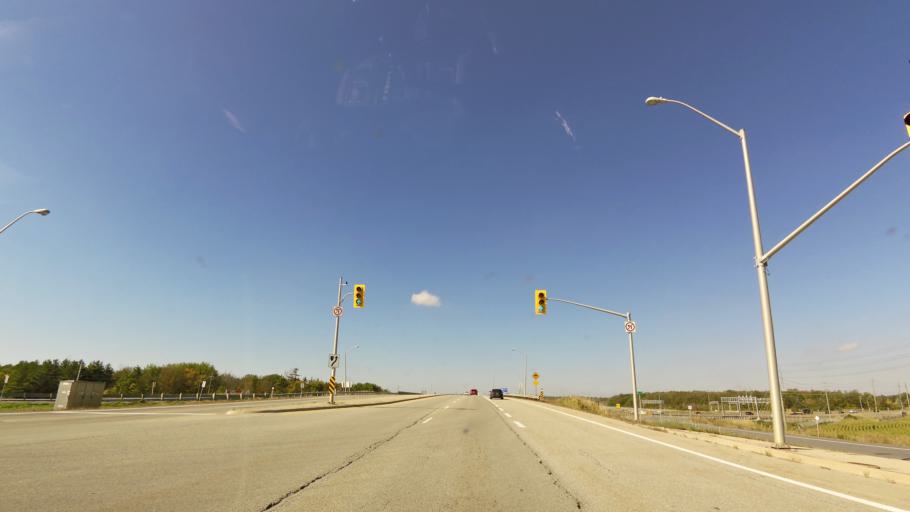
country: CA
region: Ontario
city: Burlington
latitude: 43.4441
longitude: -79.7880
